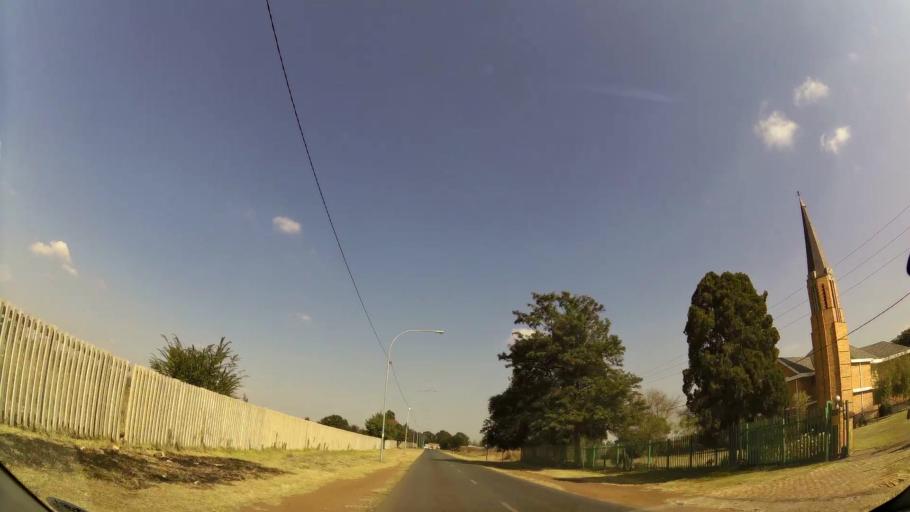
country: ZA
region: Gauteng
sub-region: Ekurhuleni Metropolitan Municipality
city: Benoni
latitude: -26.1290
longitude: 28.3925
